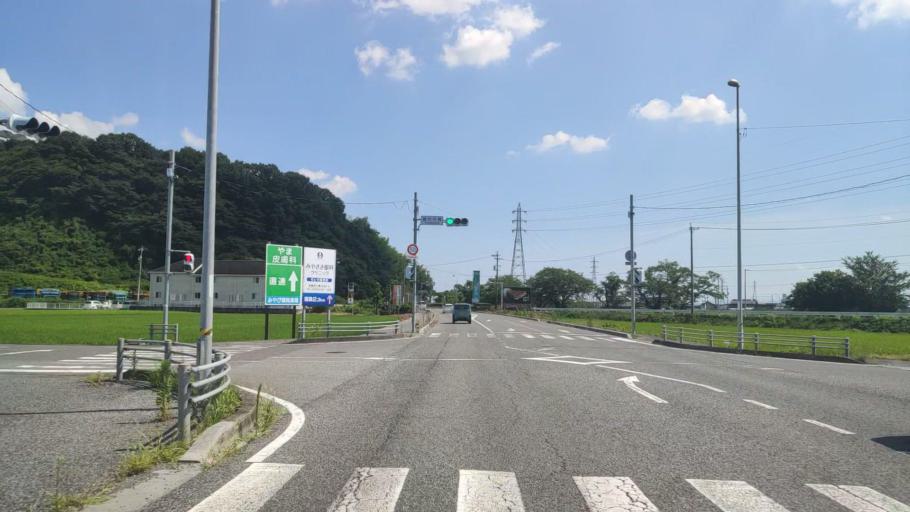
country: JP
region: Gifu
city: Godo
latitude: 35.4765
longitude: 136.6755
